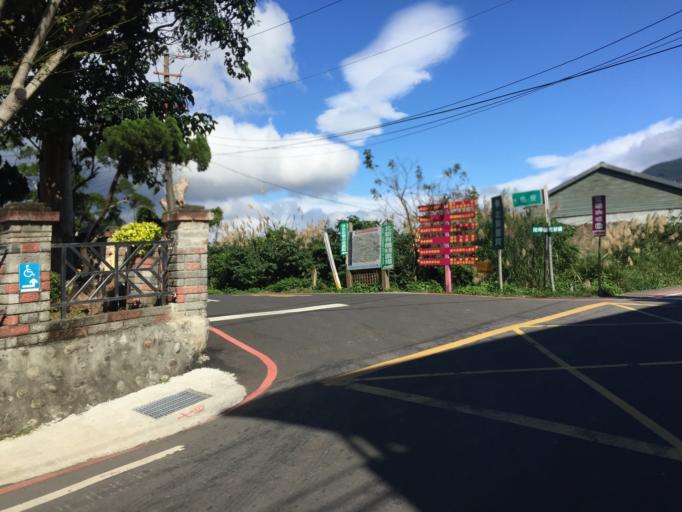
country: TW
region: Taipei
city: Taipei
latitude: 25.1858
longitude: 121.4772
